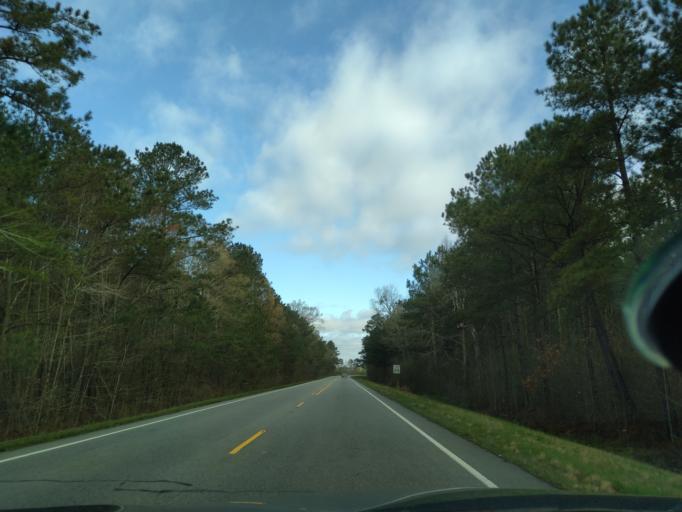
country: US
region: North Carolina
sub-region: Washington County
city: Plymouth
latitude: 35.9880
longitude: -76.7680
